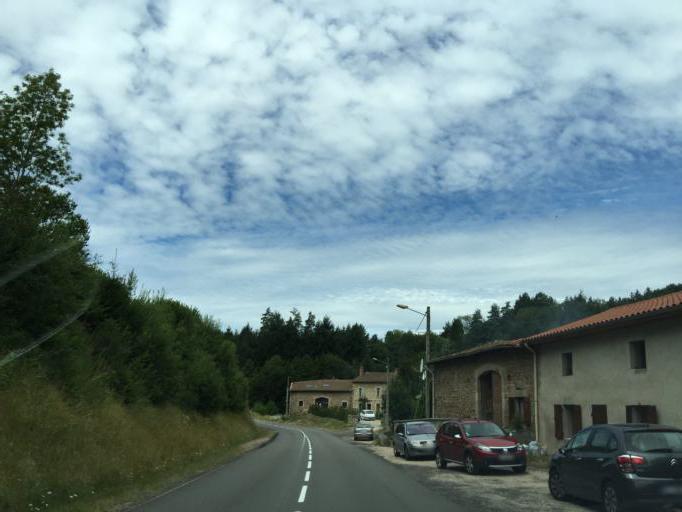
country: FR
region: Rhone-Alpes
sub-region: Departement de la Loire
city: Saint-Bonnet-le-Chateau
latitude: 45.4073
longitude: 4.1144
